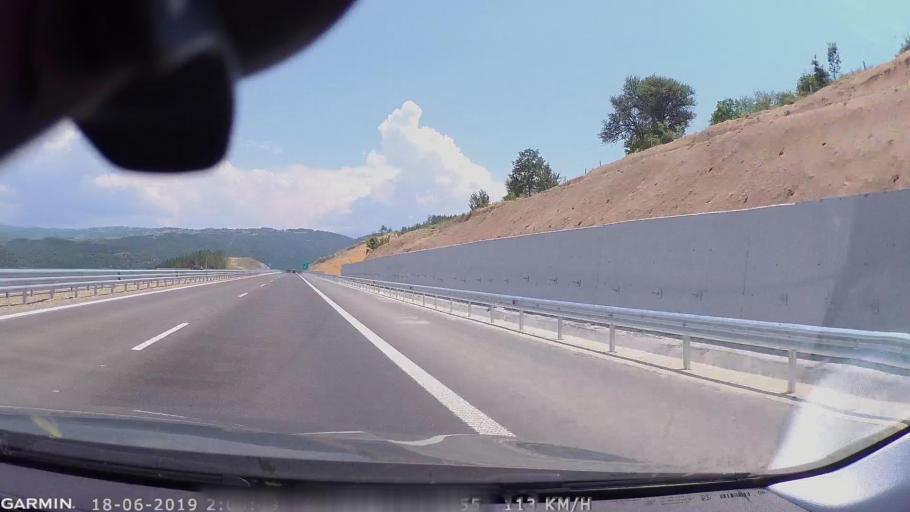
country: BG
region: Blagoevgrad
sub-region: Obshtina Blagoevgrad
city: Blagoevgrad
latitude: 41.9724
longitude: 23.0802
